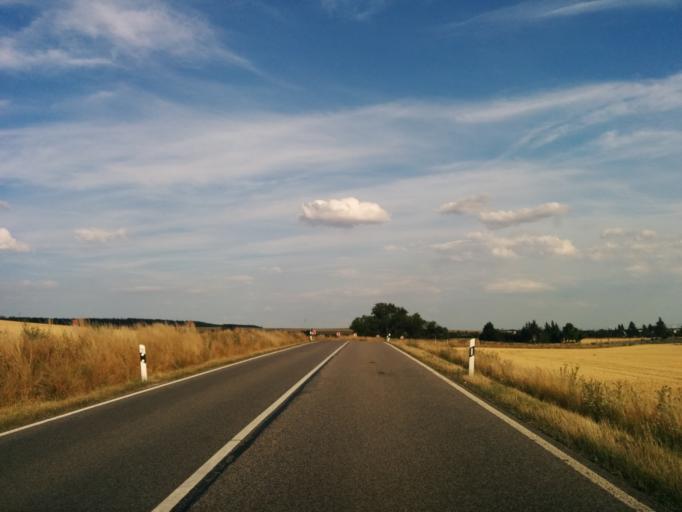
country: DE
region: Thuringia
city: Sondershausen
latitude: 51.3192
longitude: 10.8497
